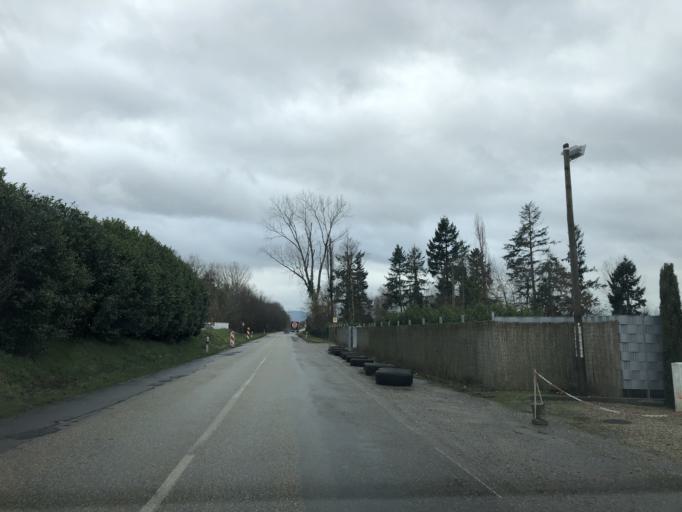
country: DE
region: Baden-Wuerttemberg
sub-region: Karlsruhe Region
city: Malsch
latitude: 48.8985
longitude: 8.3065
